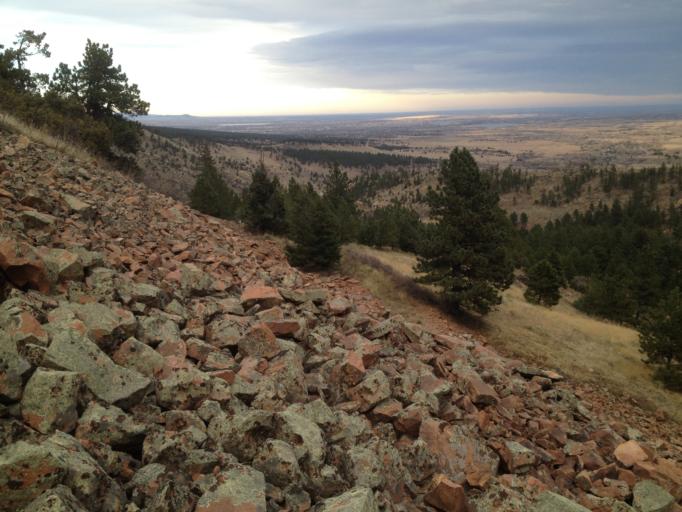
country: US
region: Colorado
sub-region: Boulder County
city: Boulder
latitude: 39.9227
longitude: -105.2802
